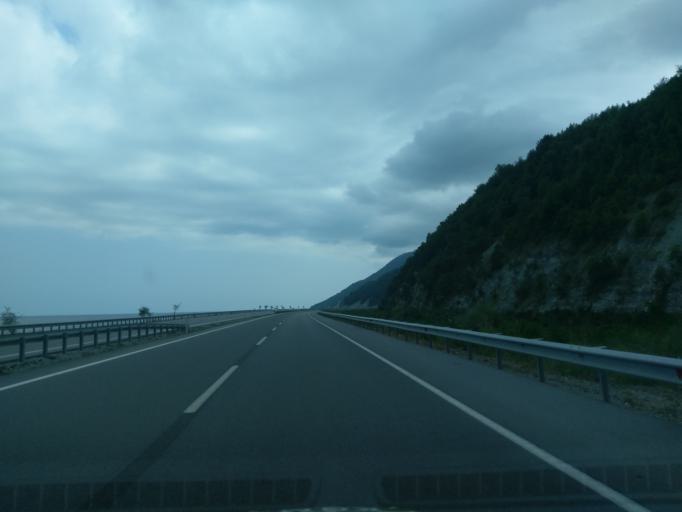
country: TR
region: Sinop
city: Dikmen
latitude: 41.7079
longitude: 35.3001
